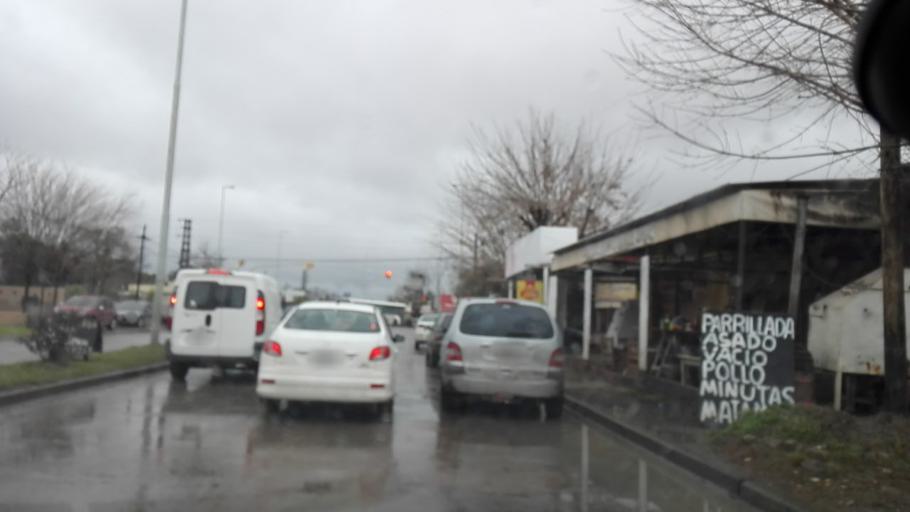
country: AR
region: Buenos Aires
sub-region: Partido de Brandsen
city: Brandsen
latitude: -35.1746
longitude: -58.2337
